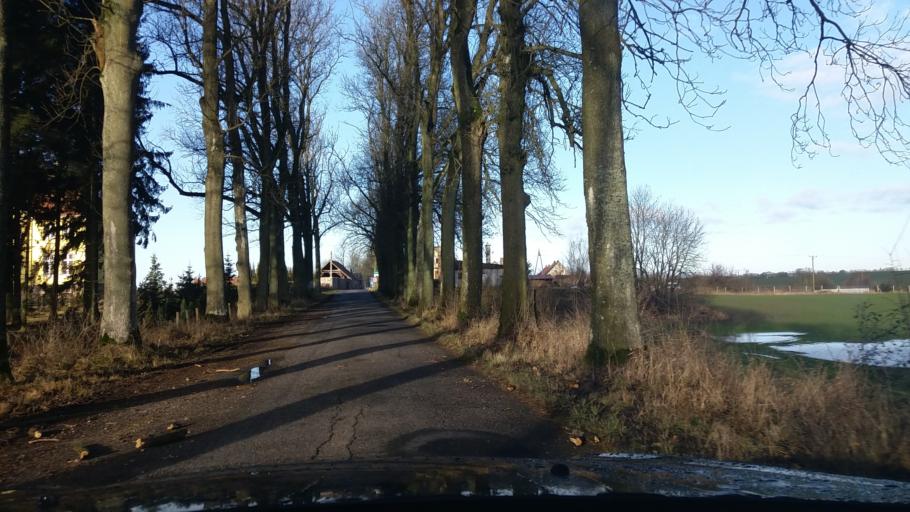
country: PL
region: West Pomeranian Voivodeship
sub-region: Powiat choszczenski
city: Drawno
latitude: 53.1921
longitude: 15.7896
